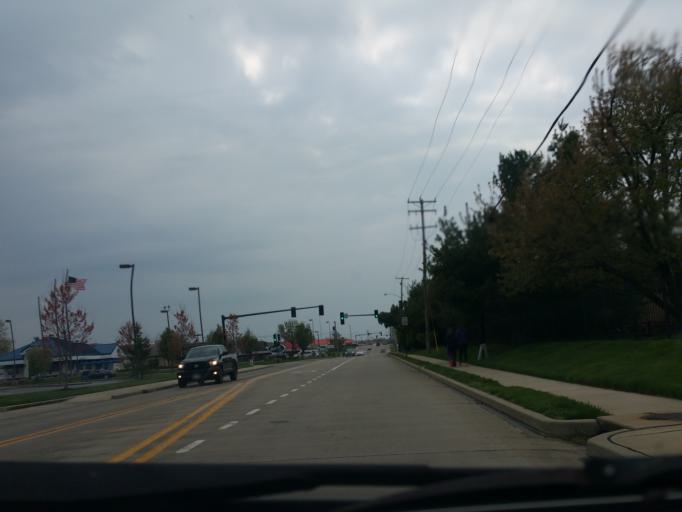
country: US
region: Illinois
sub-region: Madison County
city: Edwardsville
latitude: 38.7814
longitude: -89.9463
